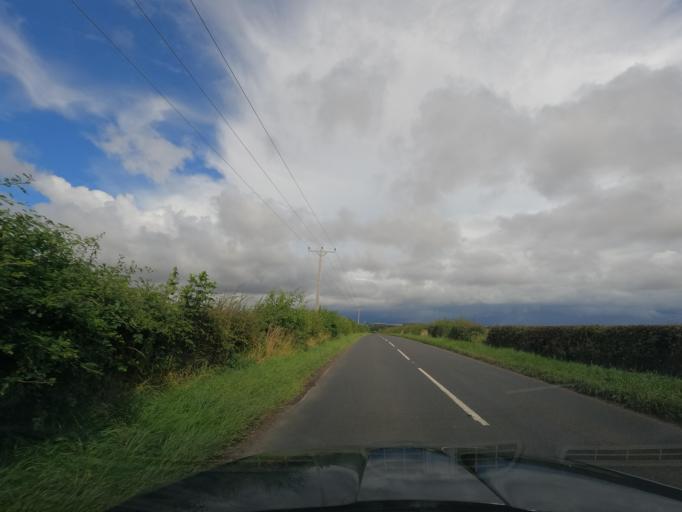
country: GB
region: England
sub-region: Northumberland
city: Ancroft
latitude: 55.6650
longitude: -1.9987
